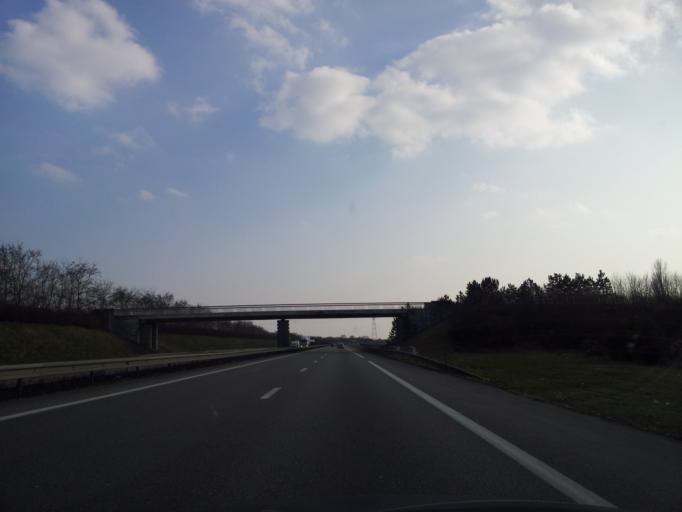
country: FR
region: Alsace
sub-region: Departement du Haut-Rhin
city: Sainte-Croix-en-Plaine
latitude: 48.0049
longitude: 7.3780
